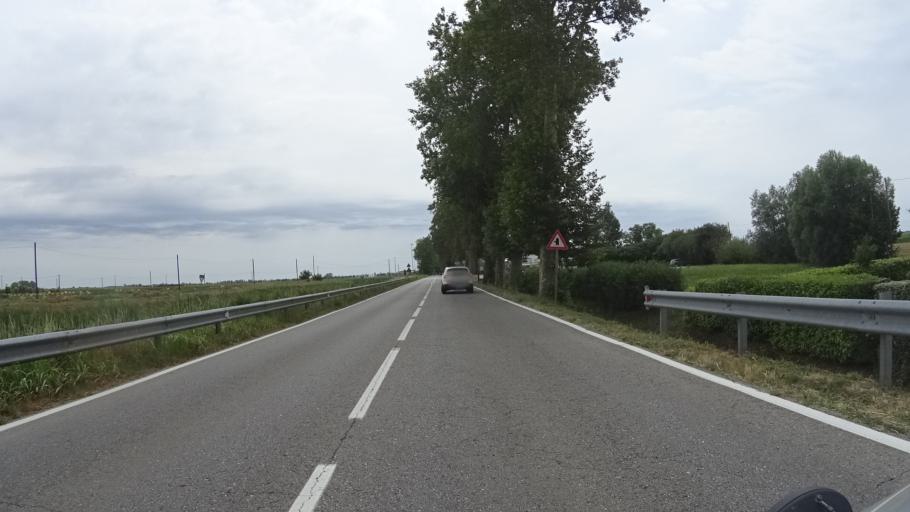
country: IT
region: Veneto
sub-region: Provincia di Venezia
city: San Giorgio di Livenza
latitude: 45.6937
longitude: 12.7678
